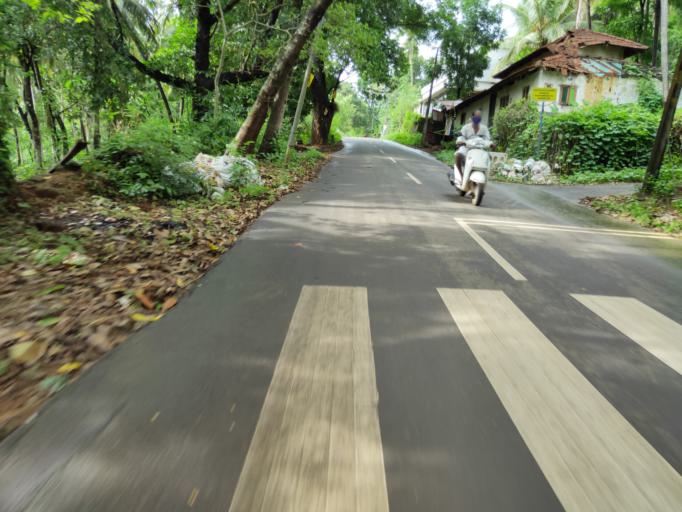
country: IN
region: Kerala
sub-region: Malappuram
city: Manjeri
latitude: 11.1367
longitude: 76.1299
